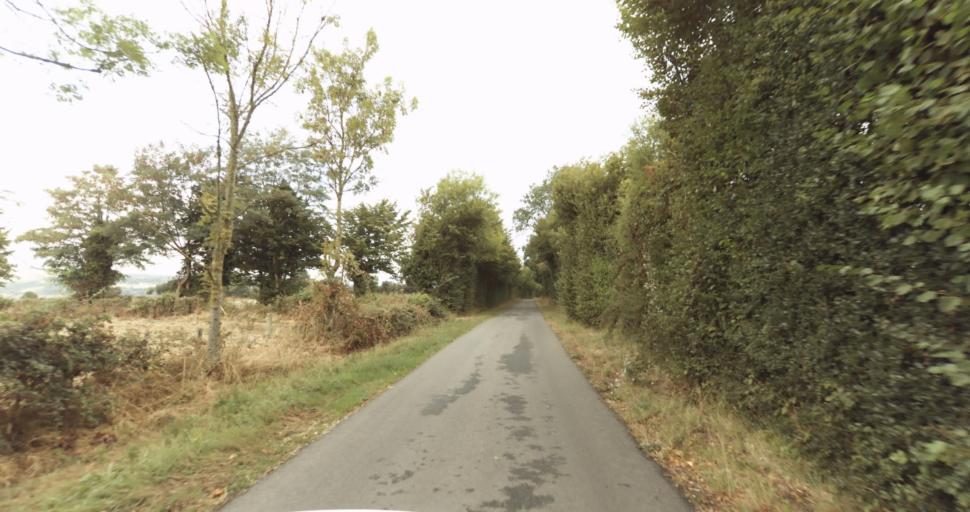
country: FR
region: Lower Normandy
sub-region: Departement de l'Orne
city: Vimoutiers
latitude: 48.9372
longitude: 0.1436
